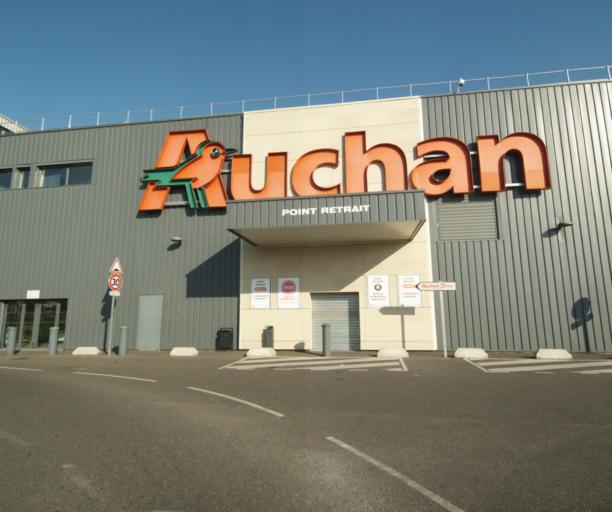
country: FR
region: Midi-Pyrenees
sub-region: Departement du Tarn-et-Garonne
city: Montauban
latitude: 44.0314
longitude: 1.3707
